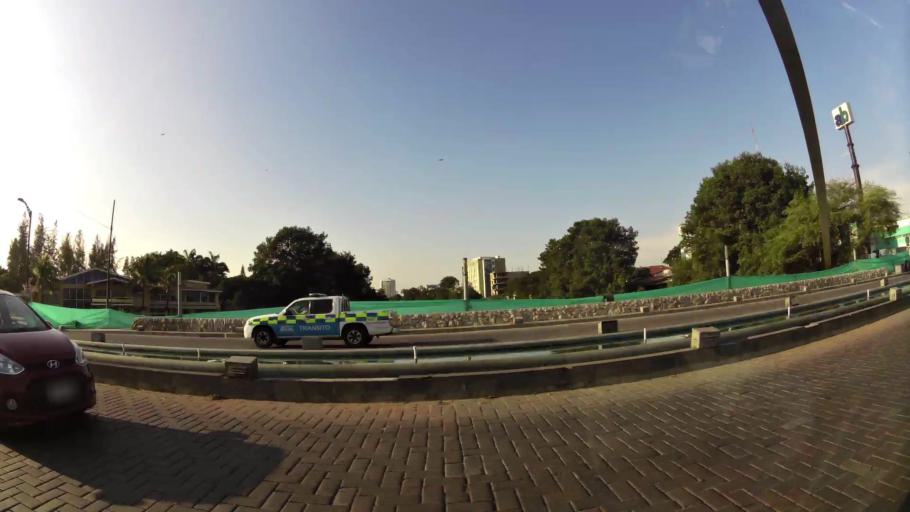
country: EC
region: Guayas
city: Guayaquil
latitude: -2.1773
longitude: -79.9036
